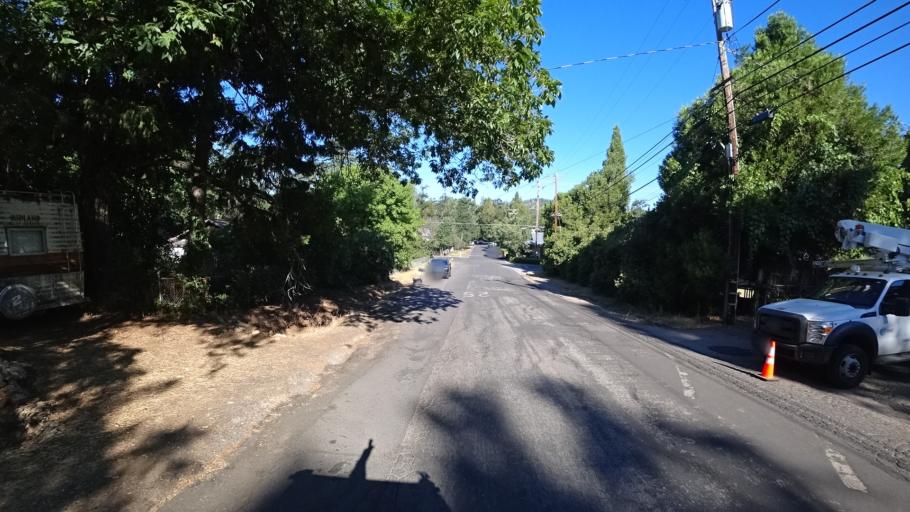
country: US
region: California
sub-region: Calaveras County
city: Murphys
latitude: 38.1365
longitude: -120.4592
